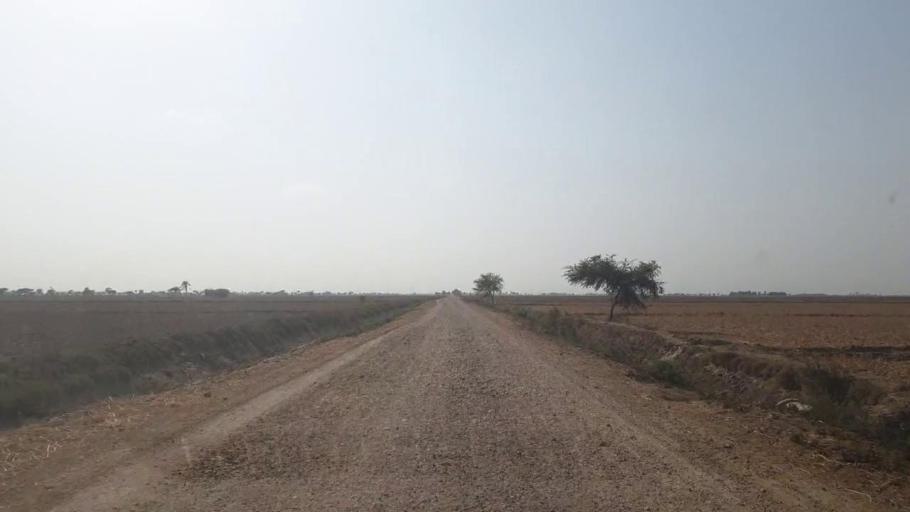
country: PK
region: Sindh
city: Kario
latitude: 24.5589
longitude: 68.5302
